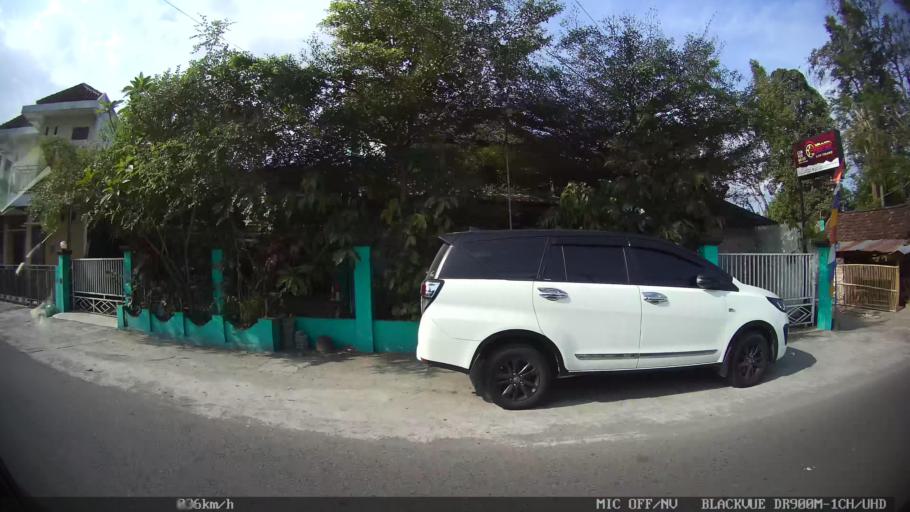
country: ID
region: Daerah Istimewa Yogyakarta
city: Kasihan
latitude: -7.8274
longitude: 110.3294
